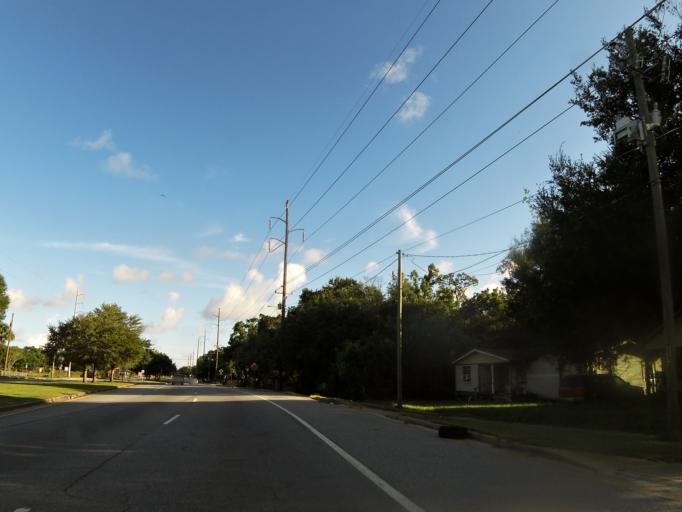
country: US
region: Georgia
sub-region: Glynn County
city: Brunswick
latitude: 31.1655
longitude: -81.4934
